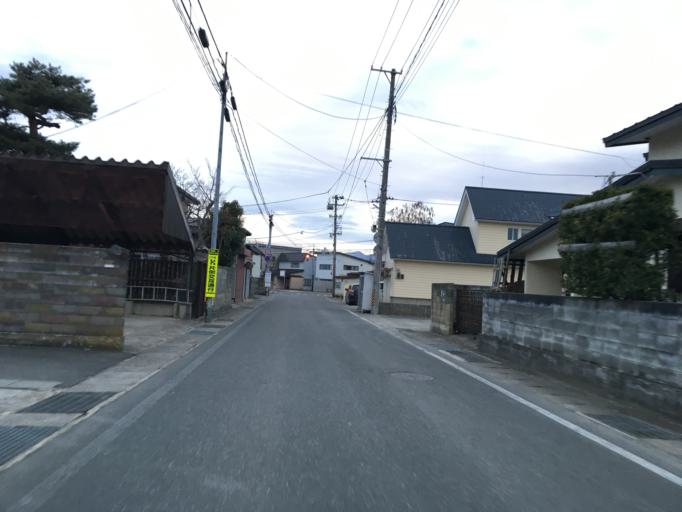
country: JP
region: Yamagata
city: Yonezawa
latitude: 37.9167
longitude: 140.0966
